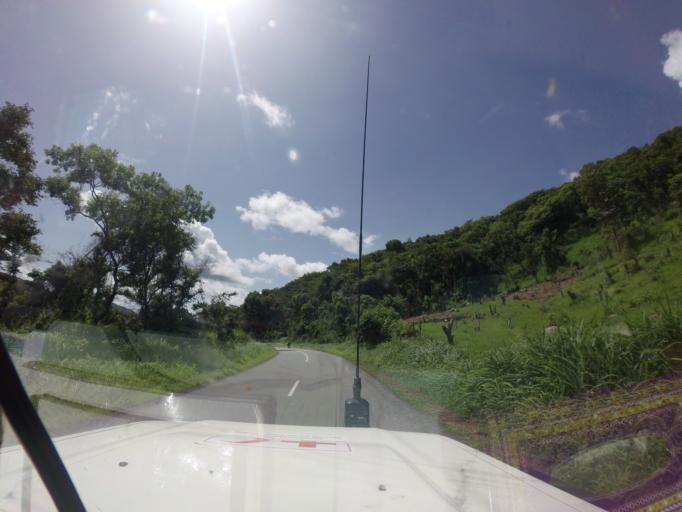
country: GN
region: Mamou
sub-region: Mamou Prefecture
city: Mamou
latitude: 10.2023
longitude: -11.8471
